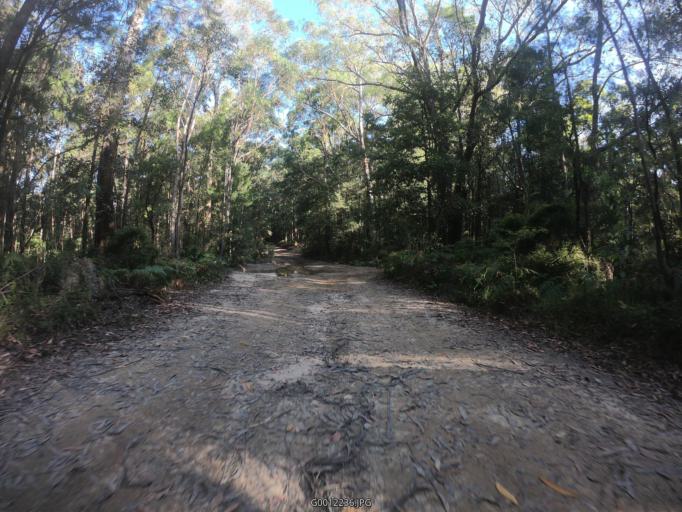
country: AU
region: New South Wales
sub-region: Lake Macquarie Shire
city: Cooranbong
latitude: -33.0848
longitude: 151.3573
